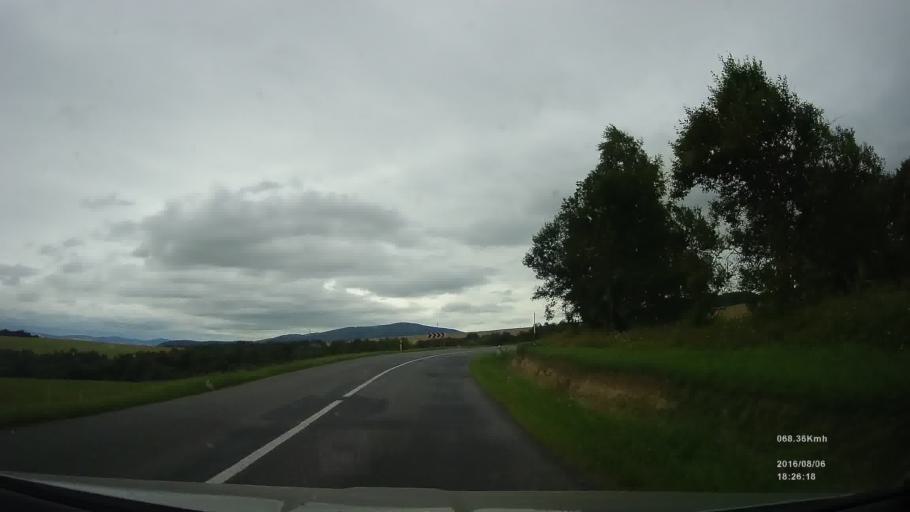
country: SK
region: Presovsky
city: Svidnik
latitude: 49.2862
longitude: 21.5719
